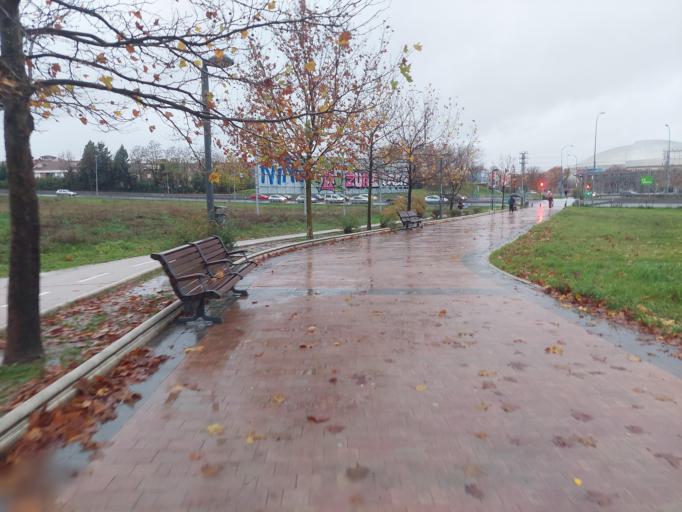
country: ES
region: Madrid
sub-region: Provincia de Madrid
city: Leganes
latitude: 40.3225
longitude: -3.7567
